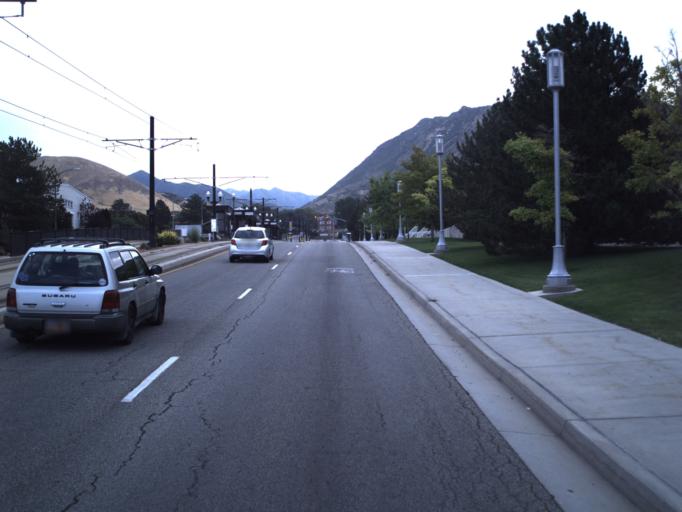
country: US
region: Utah
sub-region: Salt Lake County
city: Salt Lake City
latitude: 40.7595
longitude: -111.8410
